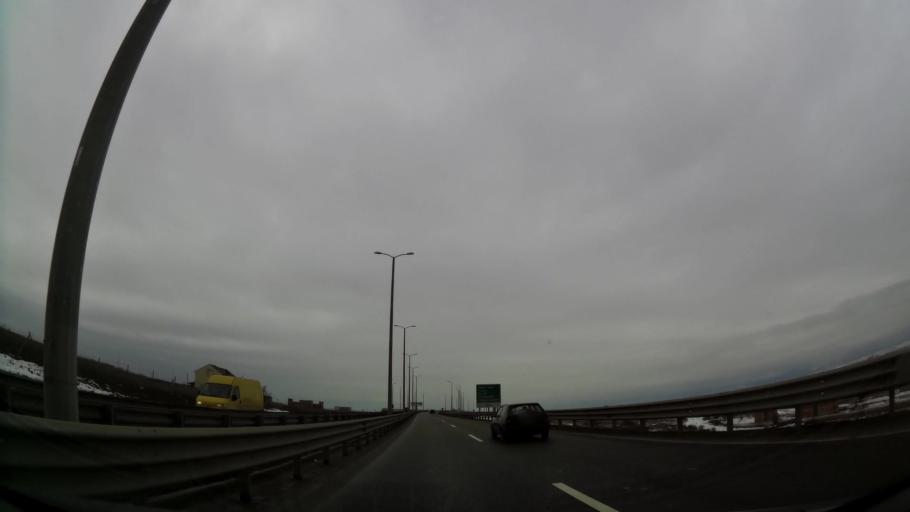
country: XK
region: Pristina
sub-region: Kosovo Polje
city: Kosovo Polje
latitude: 42.6301
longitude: 21.1361
